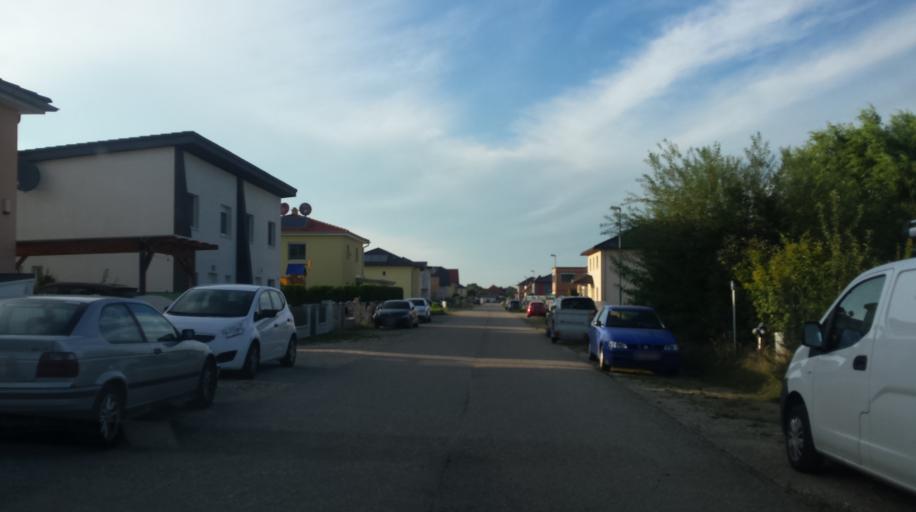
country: AT
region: Lower Austria
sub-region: Politischer Bezirk Ganserndorf
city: Strasshof an der Nordbahn
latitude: 48.3092
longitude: 16.6294
